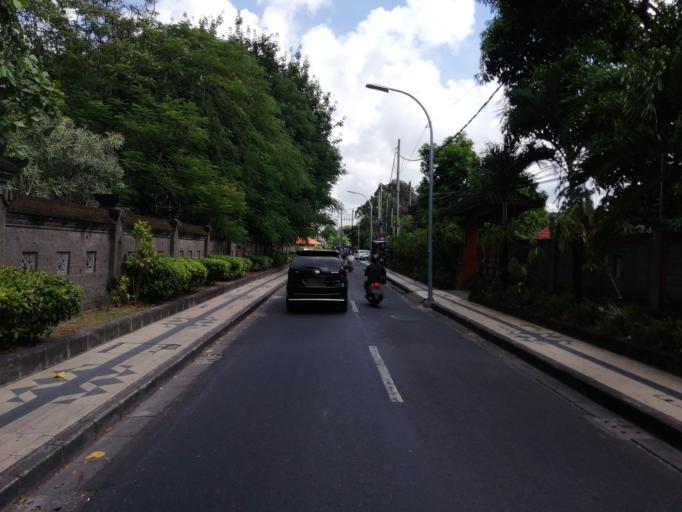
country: ID
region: Bali
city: Kuta
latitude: -8.7108
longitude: 115.1767
